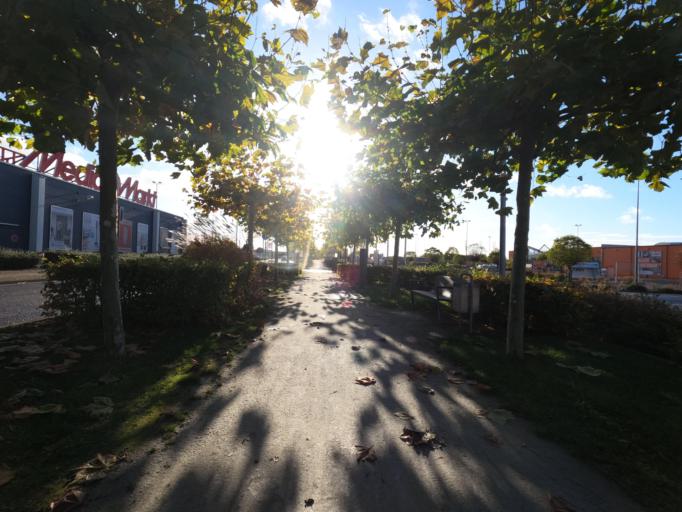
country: DE
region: North Rhine-Westphalia
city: Huckelhoven
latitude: 51.0556
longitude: 6.2188
